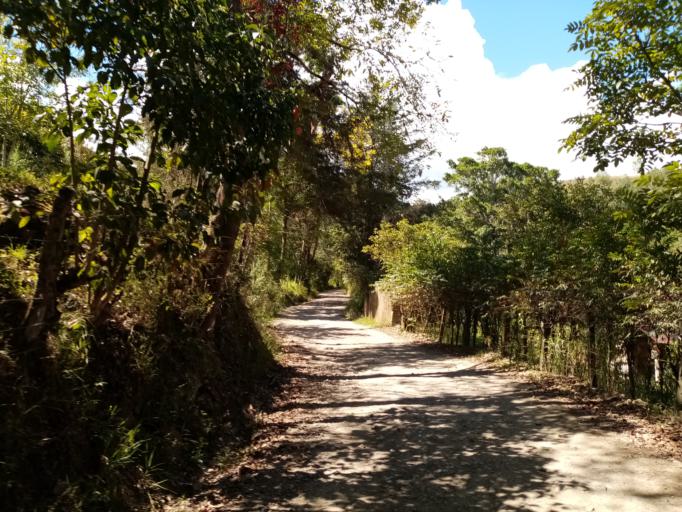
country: CO
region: Cundinamarca
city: Tenza
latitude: 5.0770
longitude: -73.4261
